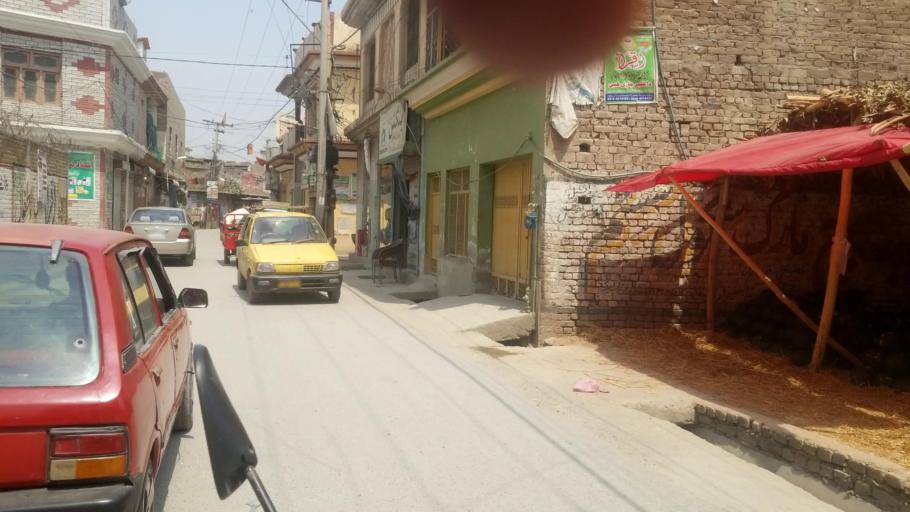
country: PK
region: Khyber Pakhtunkhwa
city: Peshawar
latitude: 34.0282
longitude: 71.5888
